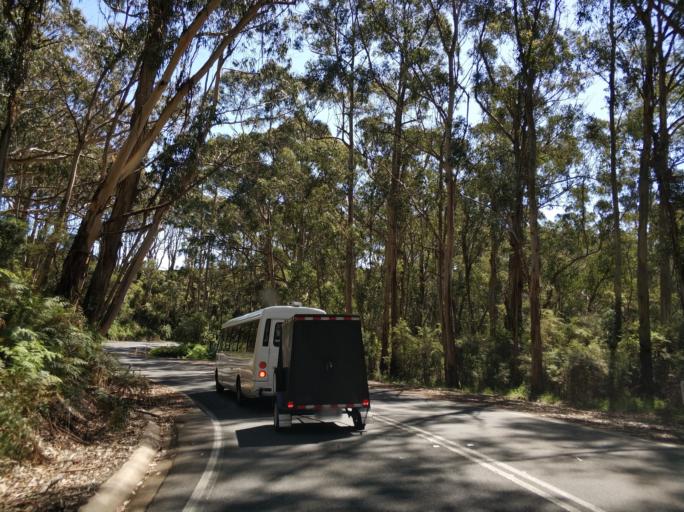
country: AU
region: Victoria
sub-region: Colac-Otway
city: Apollo Bay
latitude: -38.7420
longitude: 143.2539
